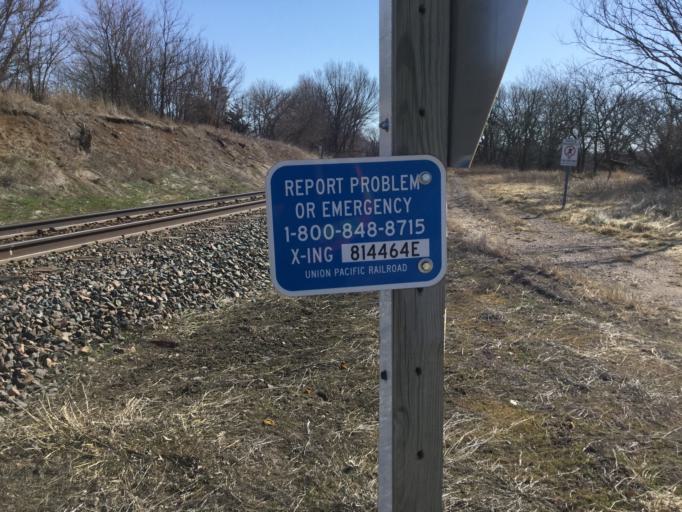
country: US
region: Kansas
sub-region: Marshall County
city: Marysville
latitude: 39.8589
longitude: -96.4265
